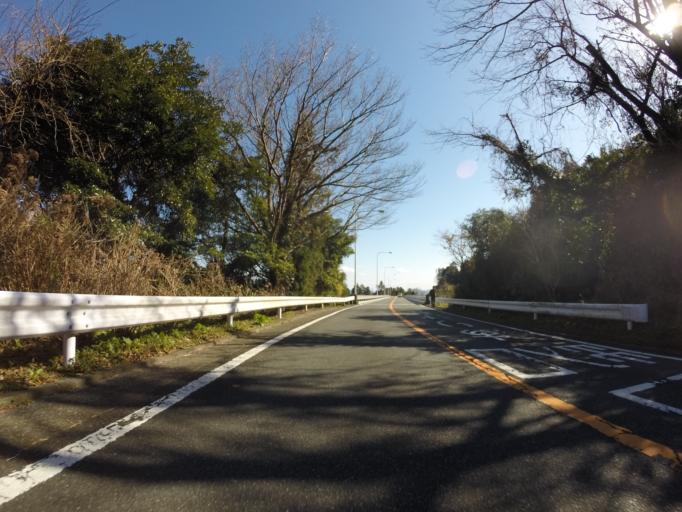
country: JP
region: Shizuoka
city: Shizuoka-shi
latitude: 34.9758
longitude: 138.4746
